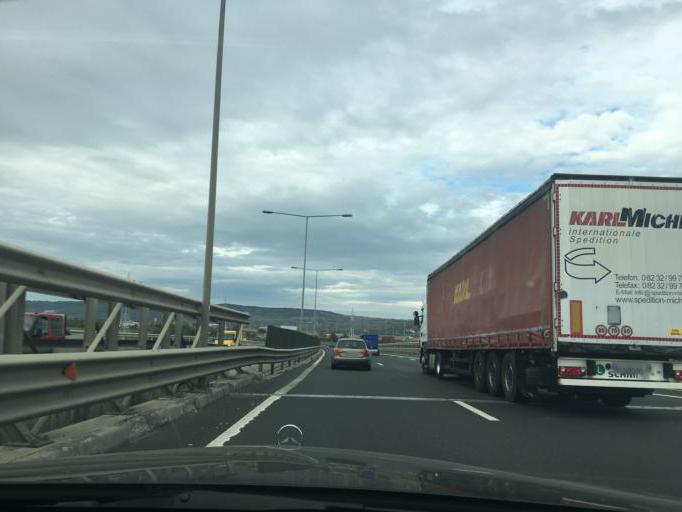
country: RO
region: Sibiu
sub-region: Comuna Selimbar
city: Selimbar
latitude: 45.7540
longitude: 24.2049
